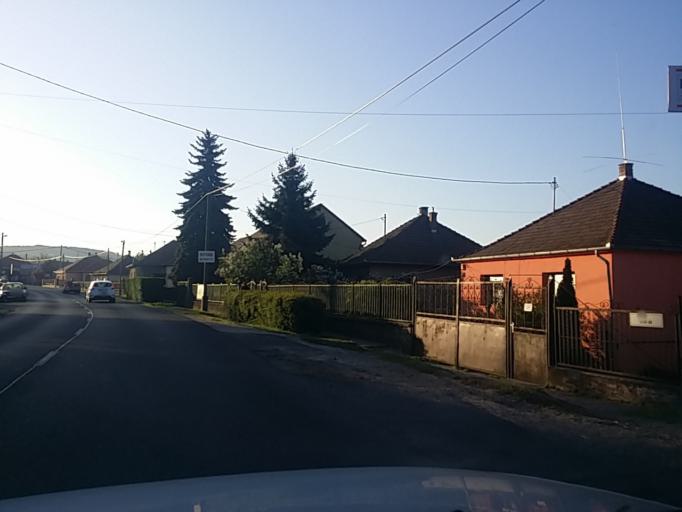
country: HU
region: Pest
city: Mogyorod
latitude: 47.5960
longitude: 19.2319
